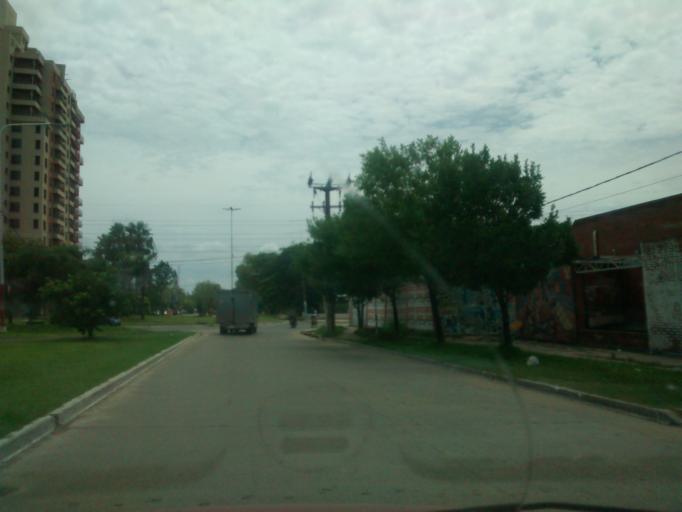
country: AR
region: Chaco
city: Resistencia
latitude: -27.4643
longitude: -58.9869
